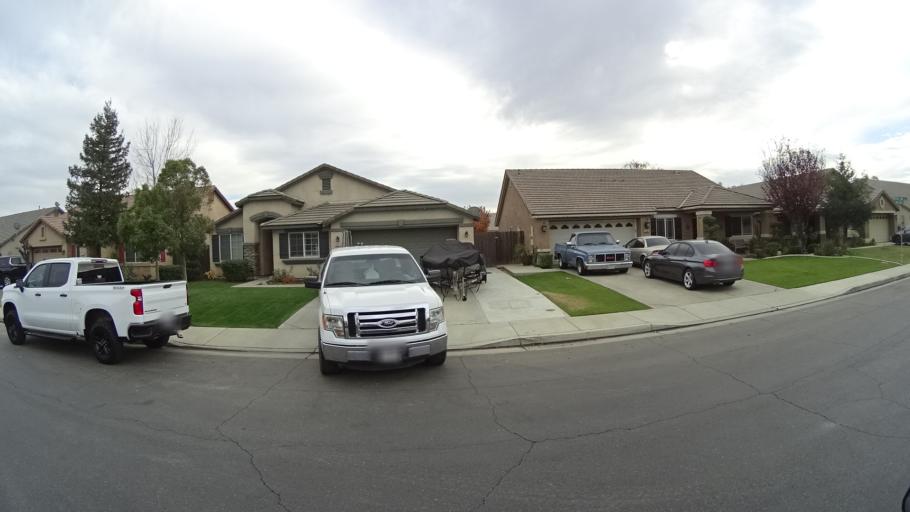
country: US
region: California
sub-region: Kern County
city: Rosedale
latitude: 35.4074
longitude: -119.1470
